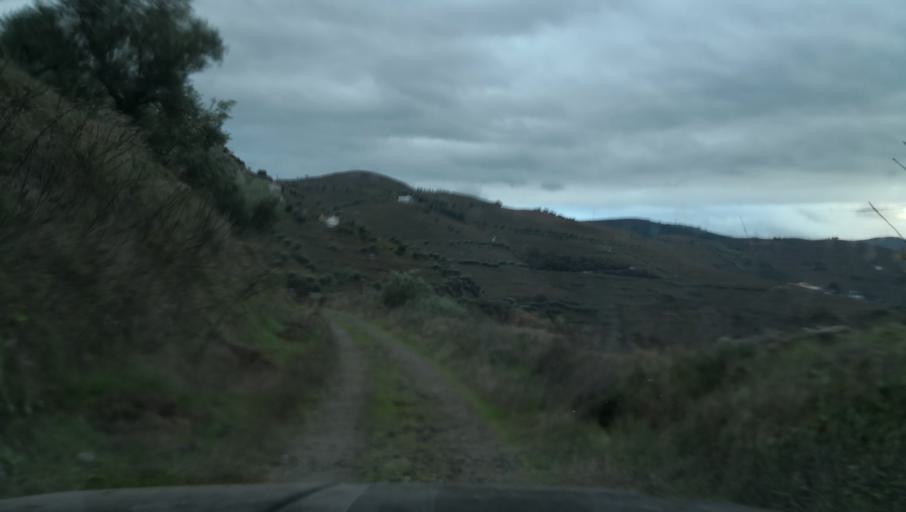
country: PT
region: Vila Real
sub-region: Peso da Regua
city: Peso da Regua
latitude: 41.1937
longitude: -7.7617
